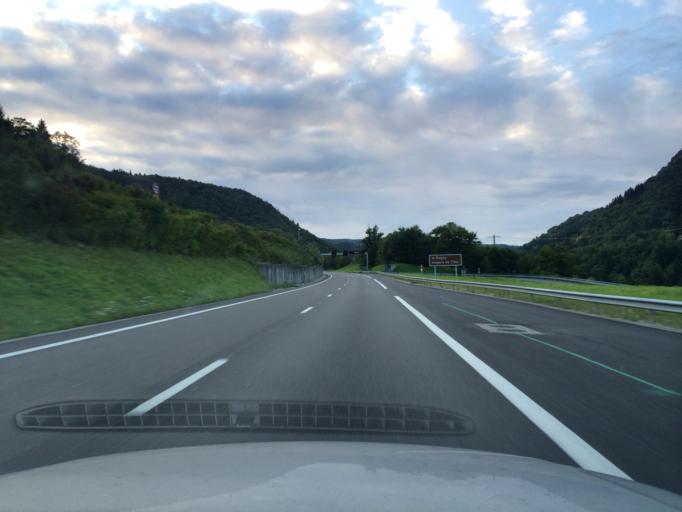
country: FR
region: Rhone-Alpes
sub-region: Departement de l'Ain
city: Chatillon-en-Michaille
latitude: 46.1677
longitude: 5.7529
